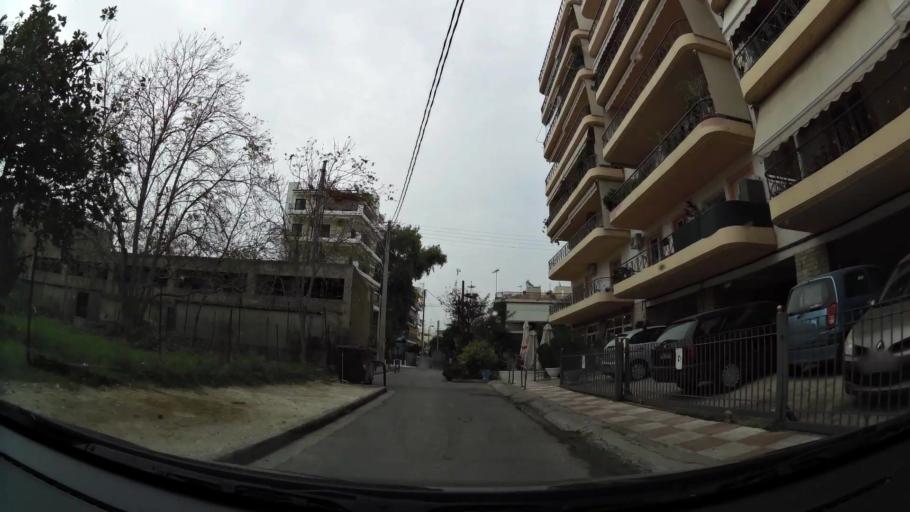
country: GR
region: Attica
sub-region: Nomos Piraios
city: Agios Ioannis Rentis
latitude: 37.9575
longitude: 23.6682
